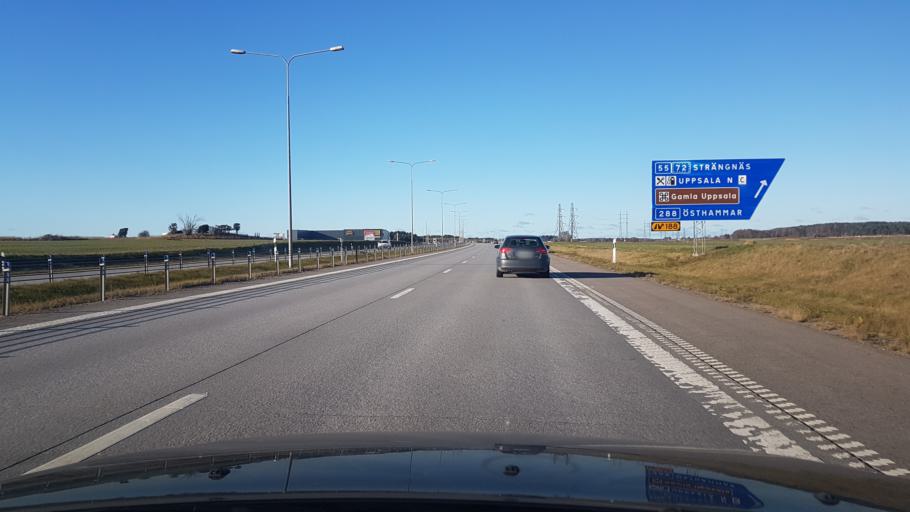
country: SE
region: Uppsala
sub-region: Uppsala Kommun
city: Uppsala
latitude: 59.8831
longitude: 17.6834
